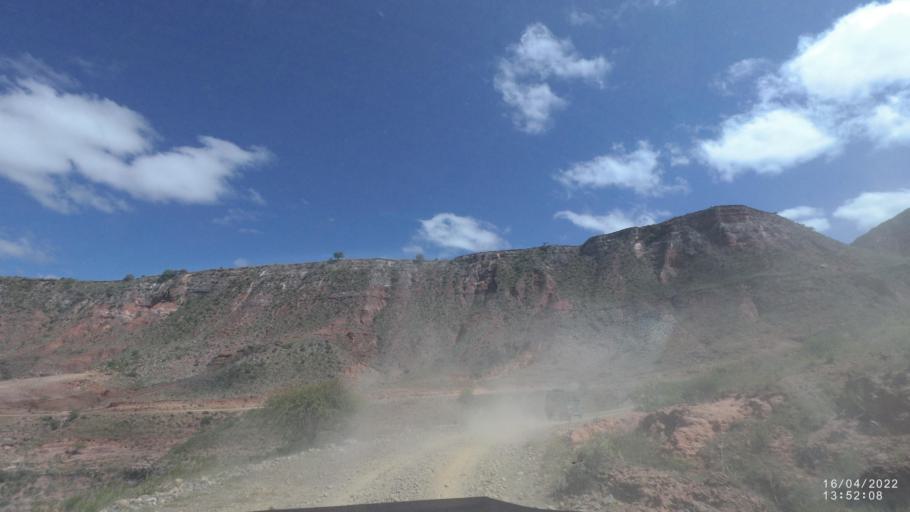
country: BO
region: Cochabamba
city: Mizque
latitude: -18.0215
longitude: -65.5733
